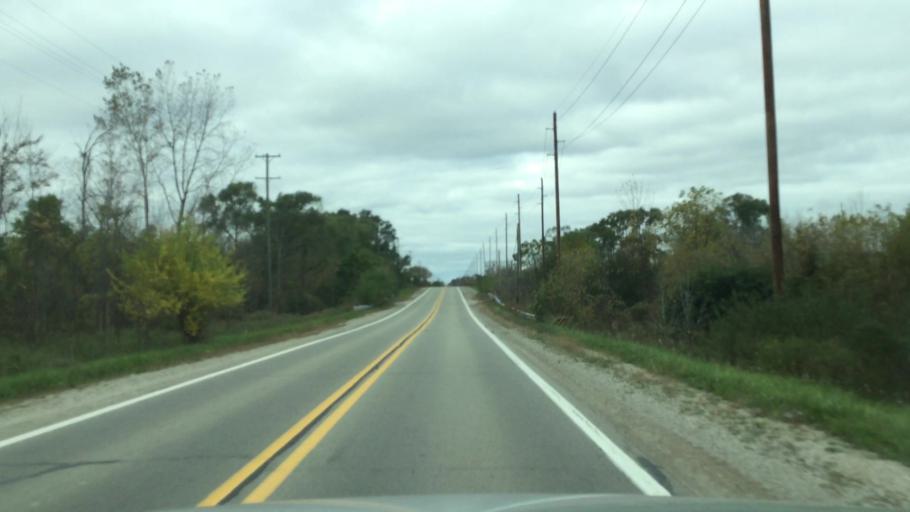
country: US
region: Michigan
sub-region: Macomb County
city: Armada
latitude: 42.8066
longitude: -82.8702
